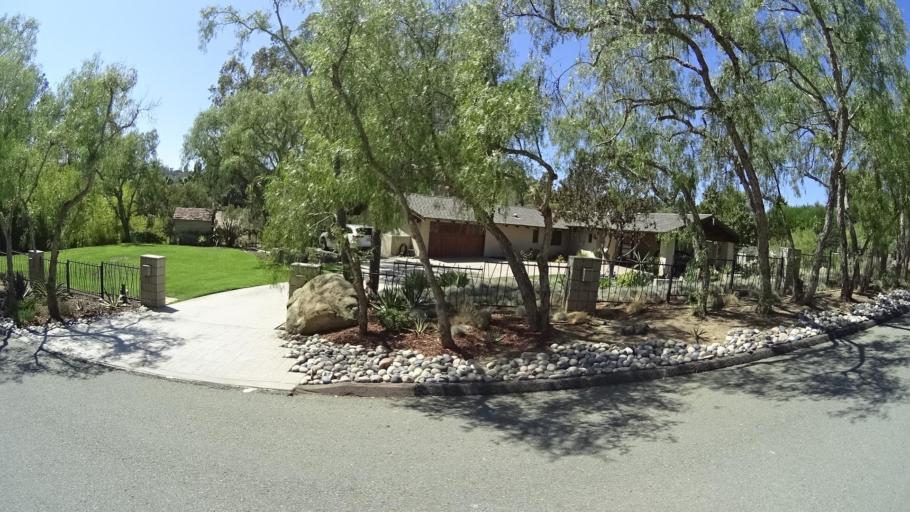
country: US
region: California
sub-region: San Diego County
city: Rancho Santa Fe
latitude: 33.0270
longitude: -117.1762
